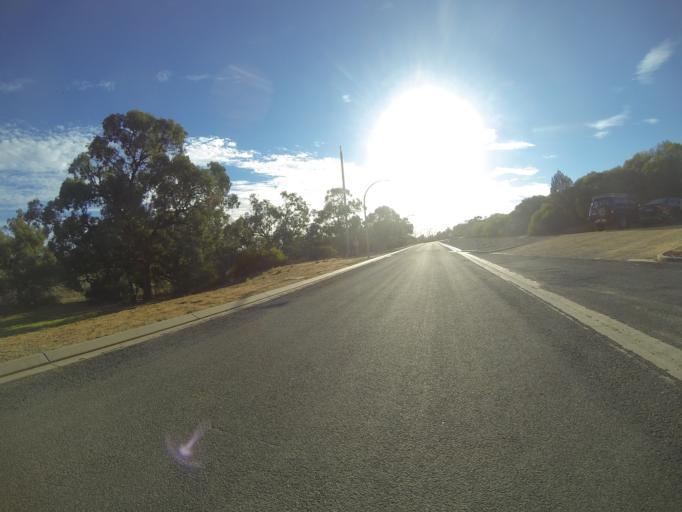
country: AU
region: South Australia
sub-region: Loxton Waikerie
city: Loxton
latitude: -34.4523
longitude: 140.5510
